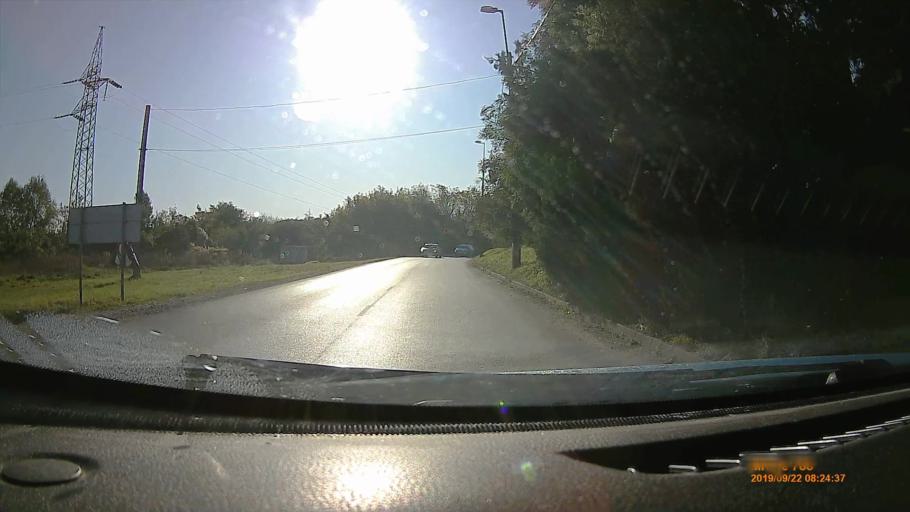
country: HU
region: Borsod-Abauj-Zemplen
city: Miskolc
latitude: 48.0900
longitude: 20.7121
